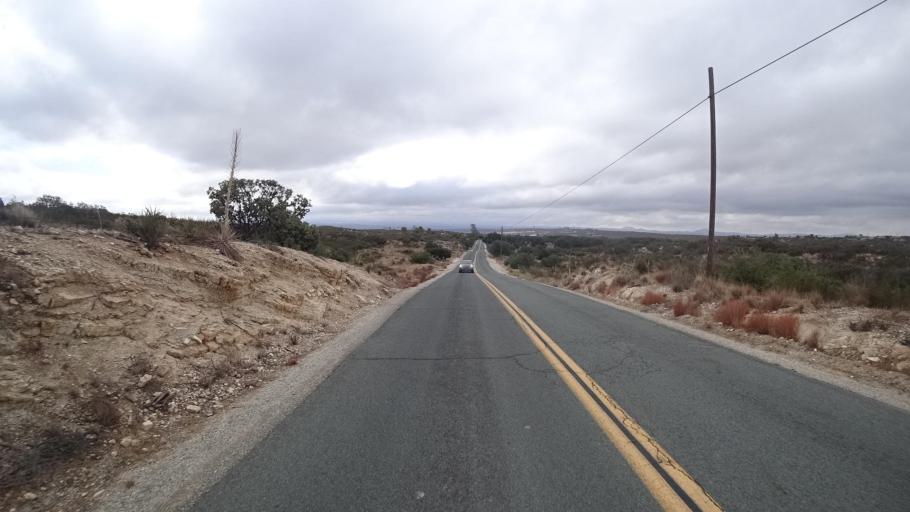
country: US
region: California
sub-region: San Diego County
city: Campo
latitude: 32.6339
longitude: -116.3201
